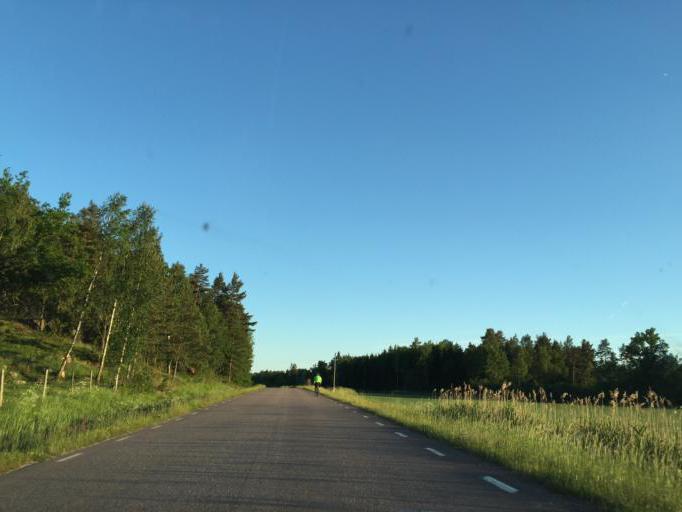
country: SE
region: Soedermanland
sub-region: Eskilstuna Kommun
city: Torshalla
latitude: 59.5223
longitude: 16.4387
